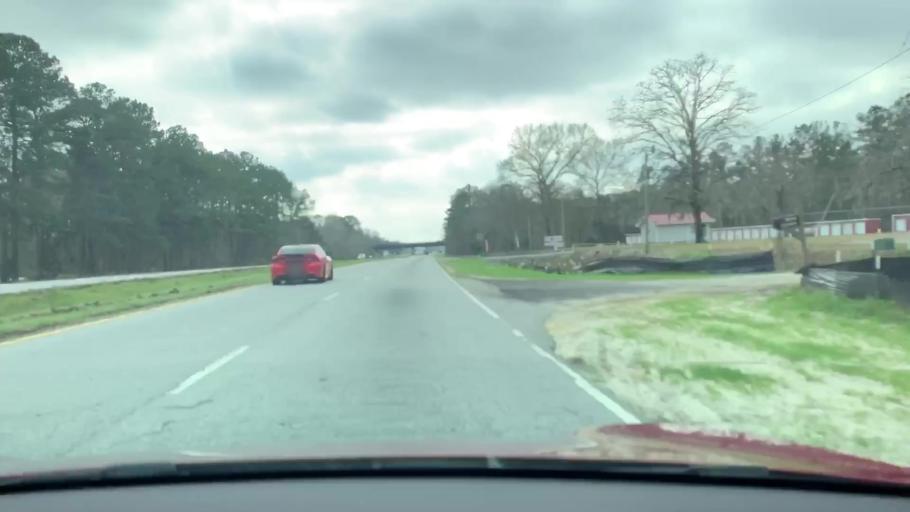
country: US
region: South Carolina
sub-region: Jasper County
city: Hardeeville
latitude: 32.2071
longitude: -81.0723
